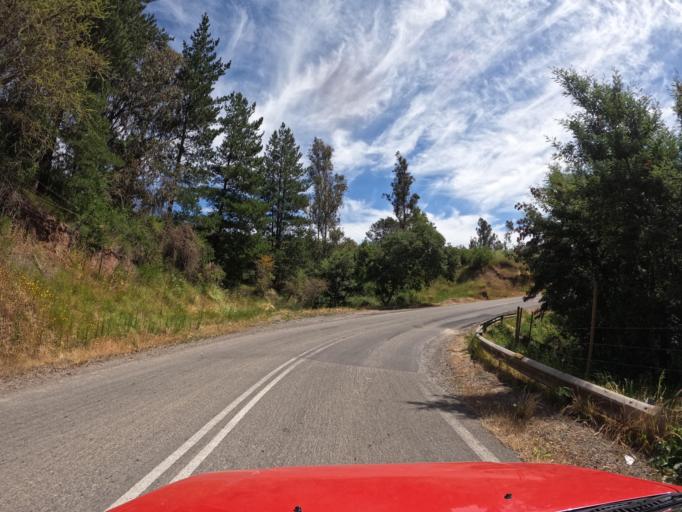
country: CL
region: Maule
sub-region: Provincia de Talca
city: Talca
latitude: -34.9917
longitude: -71.8523
